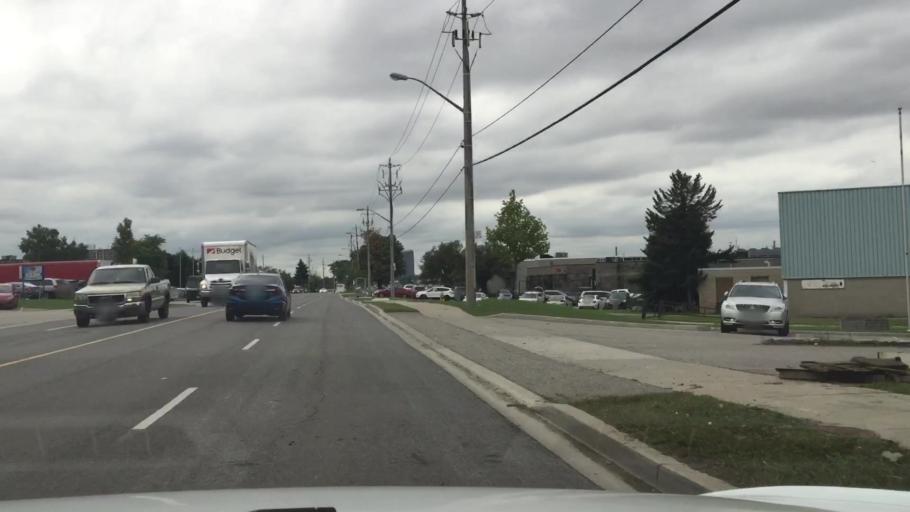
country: CA
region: Ontario
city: Scarborough
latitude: 43.7958
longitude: -79.2523
